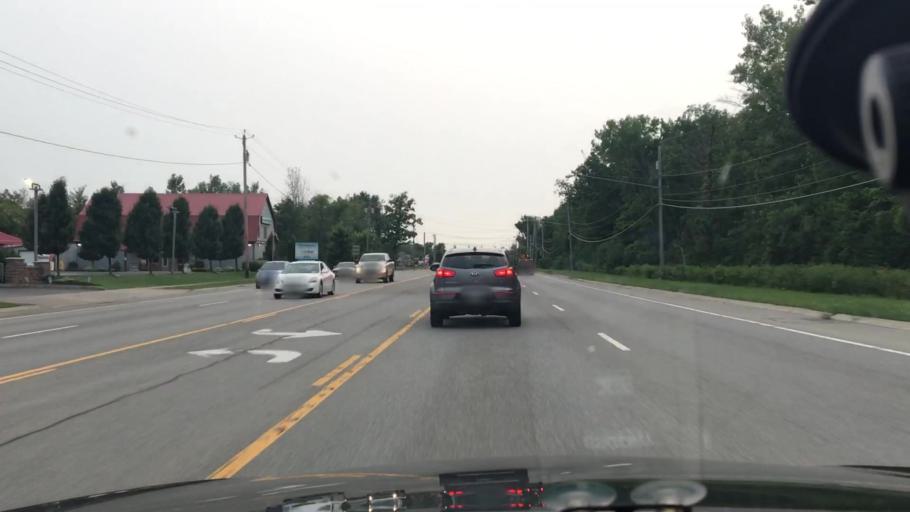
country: US
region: New York
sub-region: Erie County
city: Hamburg
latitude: 42.7569
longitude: -78.8406
